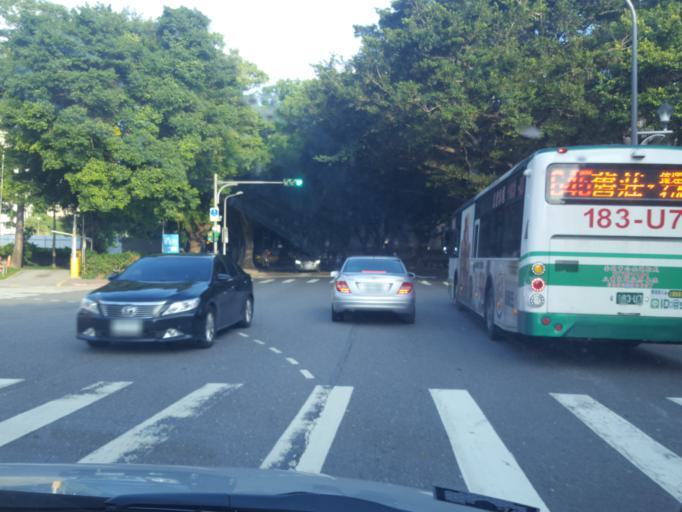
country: TW
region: Taipei
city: Taipei
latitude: 25.1187
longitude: 121.5197
